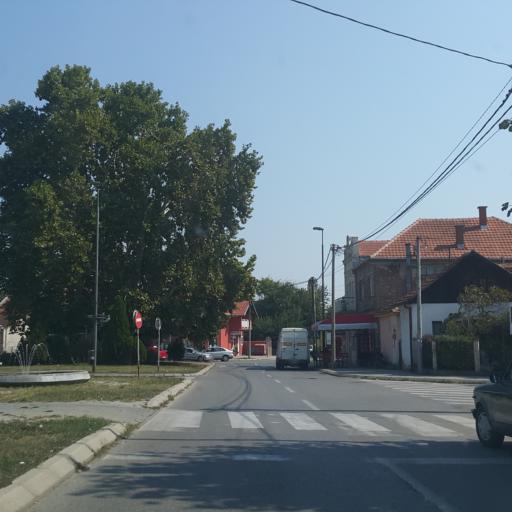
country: RS
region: Central Serbia
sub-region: Zajecarski Okrug
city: Zajecar
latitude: 43.9066
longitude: 22.2860
